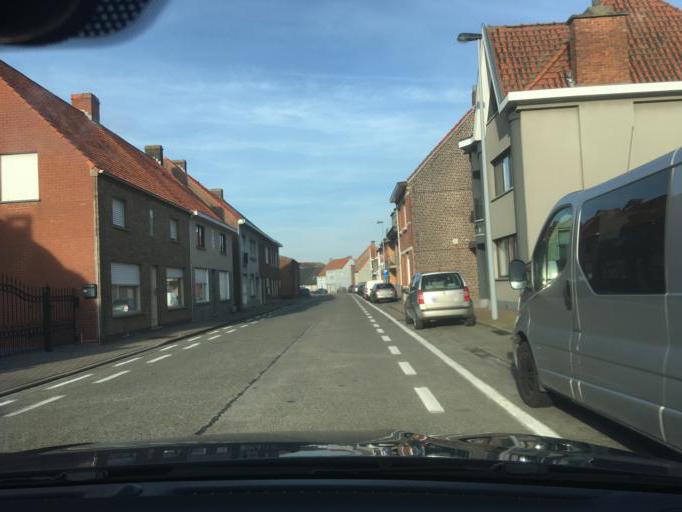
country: BE
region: Flanders
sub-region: Provincie West-Vlaanderen
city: Wielsbeke
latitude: 50.9098
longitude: 3.3677
